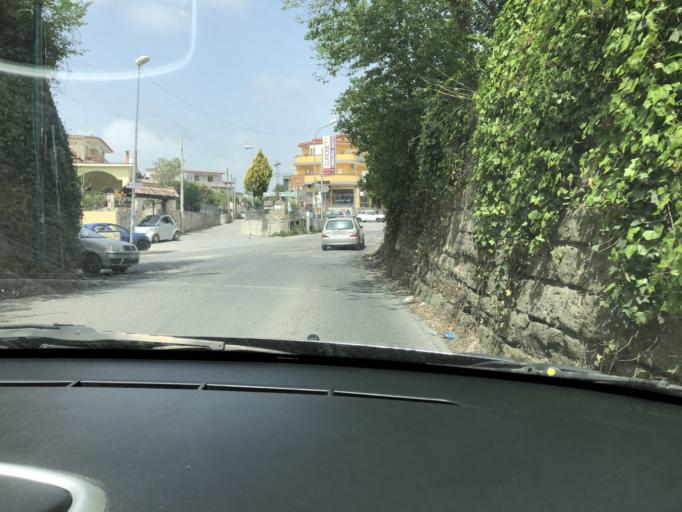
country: IT
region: Campania
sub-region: Provincia di Napoli
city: Torre Caracciolo
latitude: 40.8759
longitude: 14.1860
